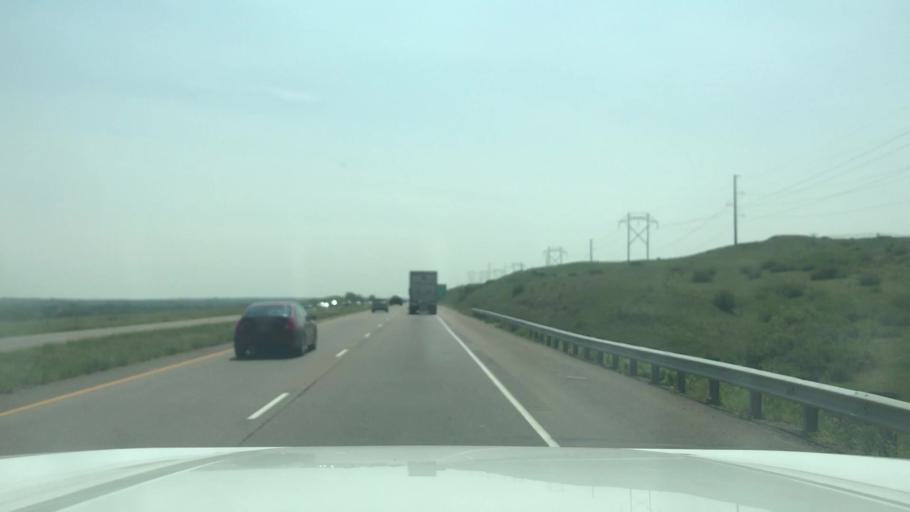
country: US
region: Colorado
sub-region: El Paso County
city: Security-Widefield
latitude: 38.7426
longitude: -104.7511
